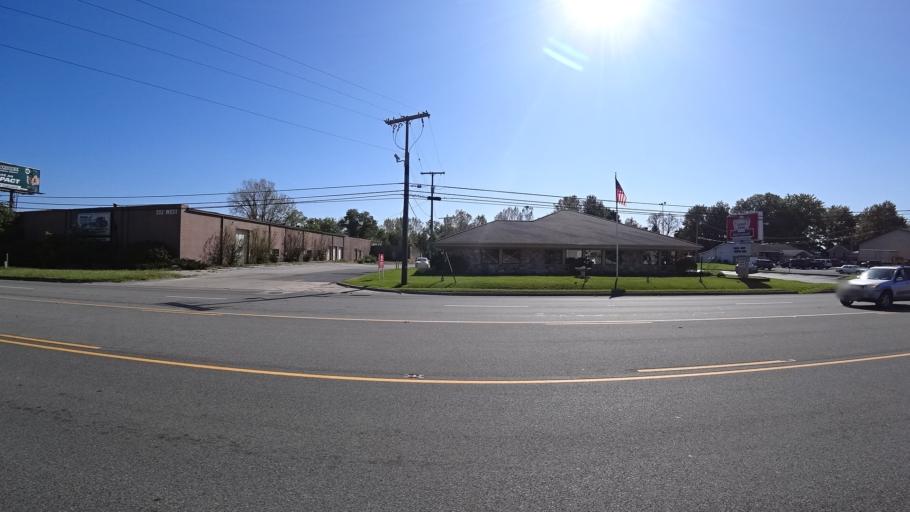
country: US
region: Indiana
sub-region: LaPorte County
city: Michigan City
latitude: 41.6805
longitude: -86.9013
